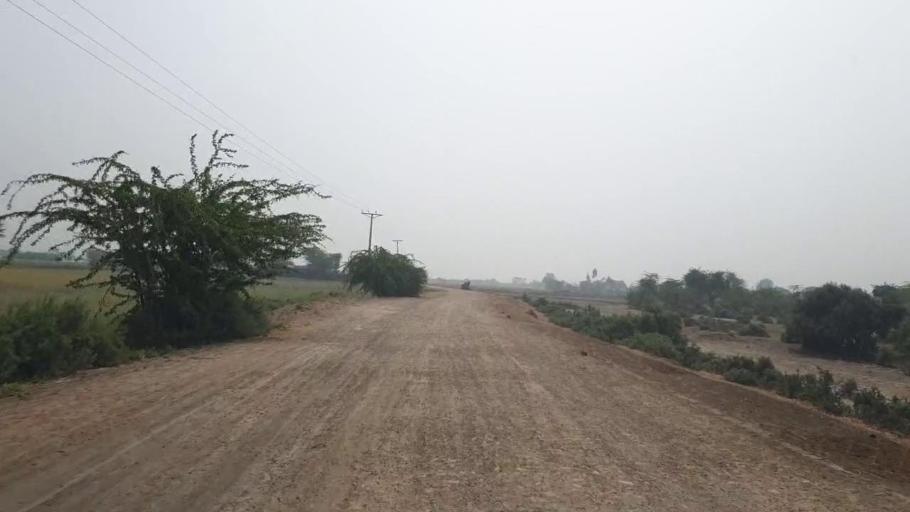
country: PK
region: Sindh
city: Kario
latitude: 24.6423
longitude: 68.6403
